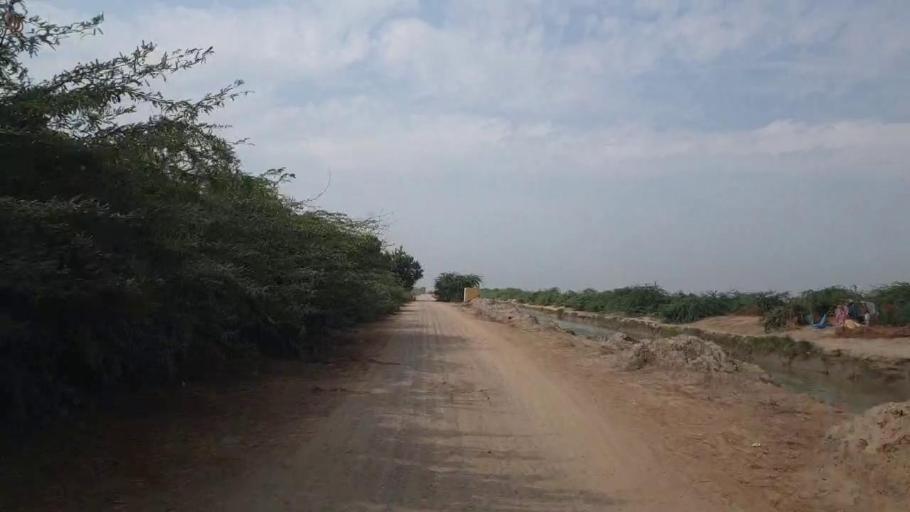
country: PK
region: Sindh
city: Kario
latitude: 24.6233
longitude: 68.5794
